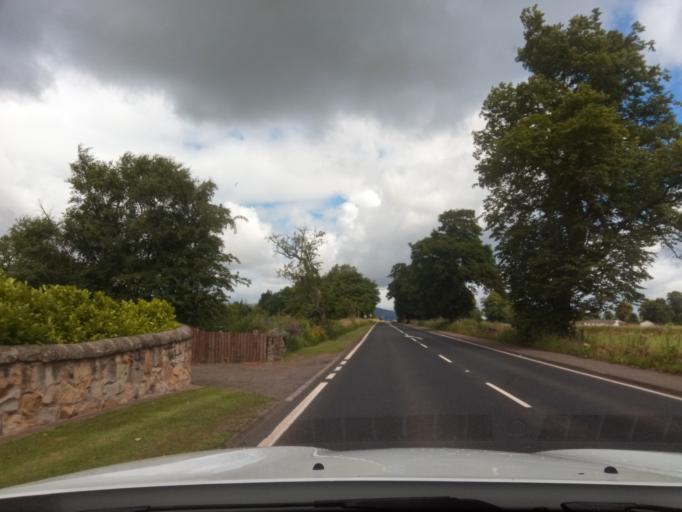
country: GB
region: Scotland
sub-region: Fife
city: Kincardine
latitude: 56.0901
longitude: -3.7189
